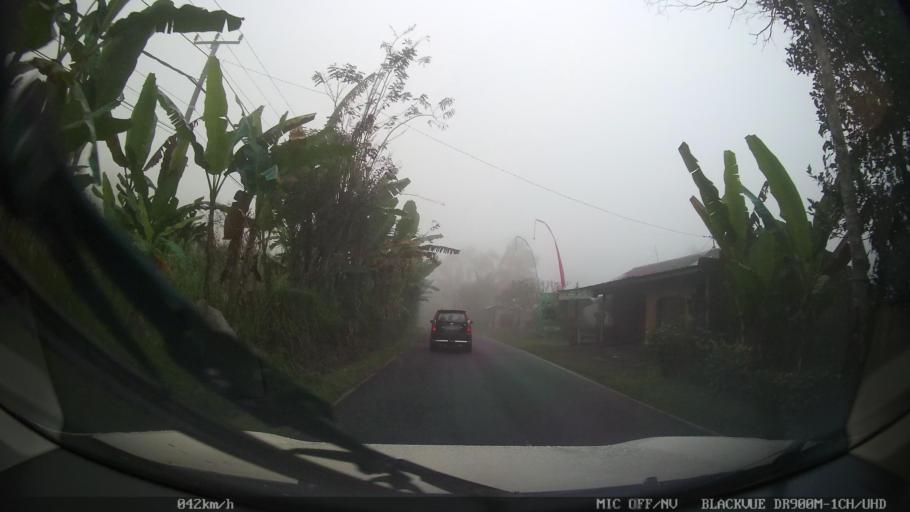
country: ID
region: Bali
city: Banjar Taro Kelod
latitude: -8.3297
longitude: 115.2884
